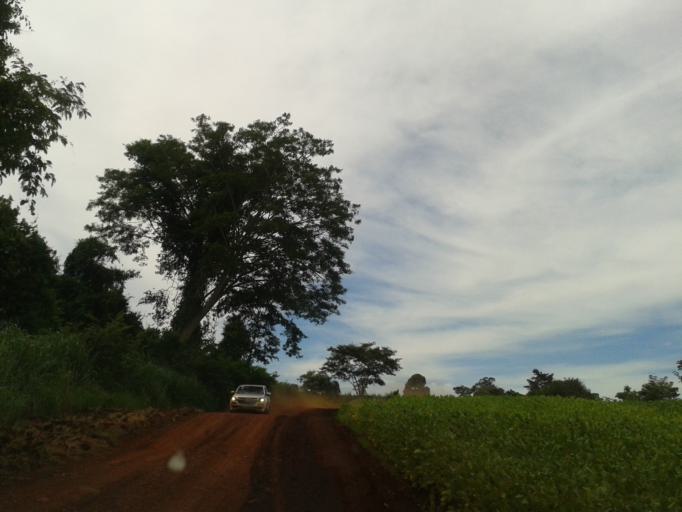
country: BR
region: Minas Gerais
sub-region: Capinopolis
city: Capinopolis
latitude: -18.7622
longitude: -49.8078
